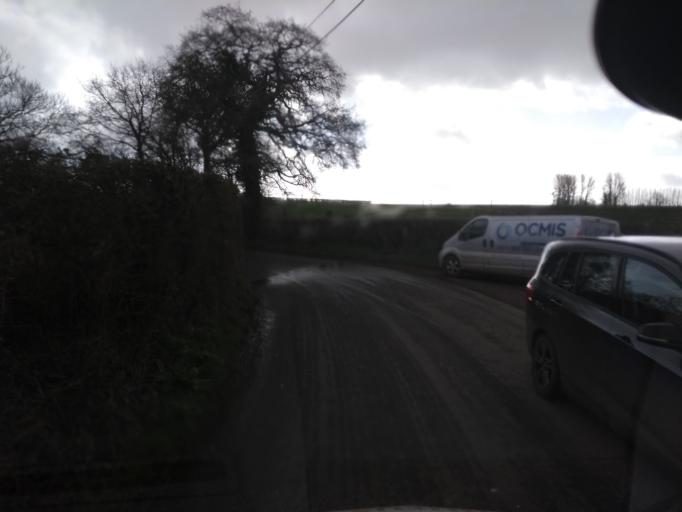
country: GB
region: England
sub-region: Somerset
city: South Petherton
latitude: 50.9753
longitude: -2.8436
